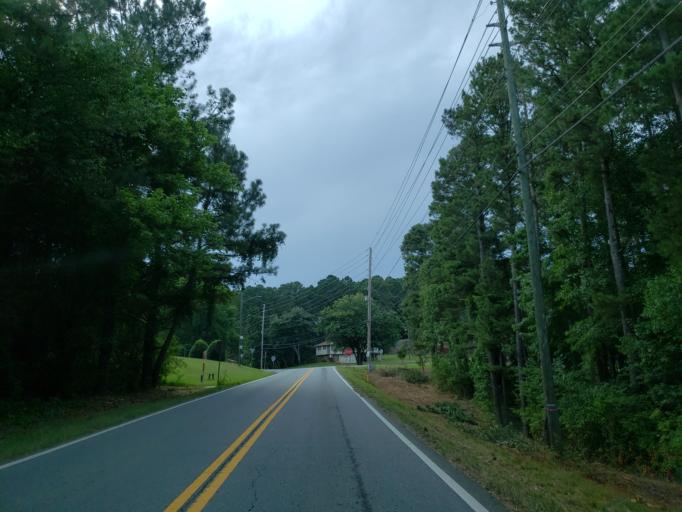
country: US
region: Georgia
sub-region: Cherokee County
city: Holly Springs
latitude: 34.1253
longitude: -84.4093
